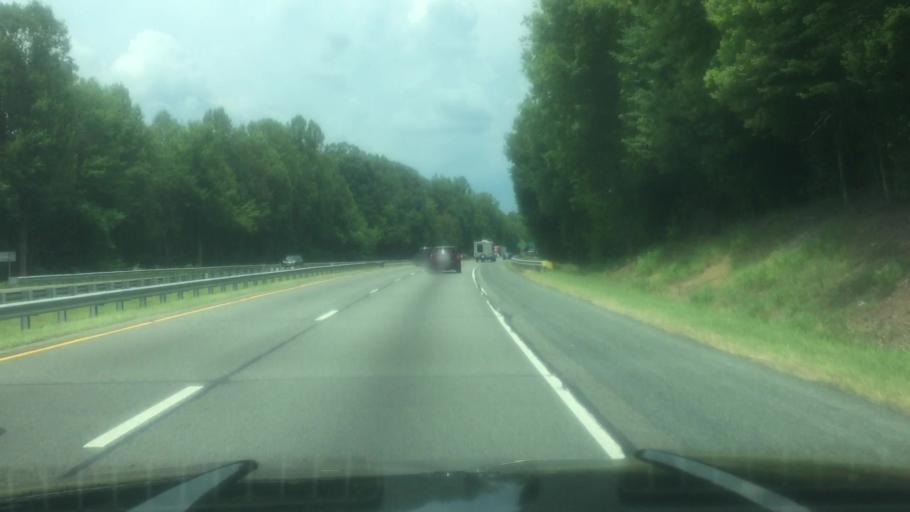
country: US
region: North Carolina
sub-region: Surry County
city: Pilot Mountain
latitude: 36.3252
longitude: -80.4493
